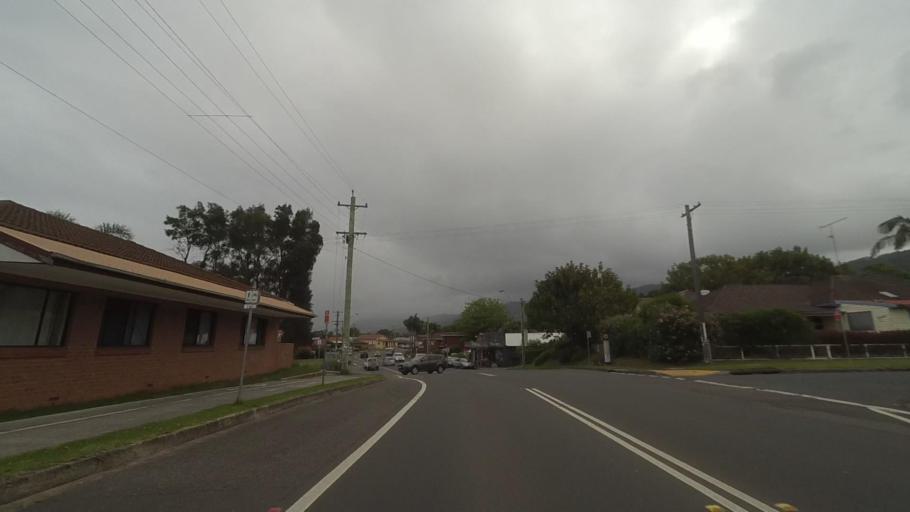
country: AU
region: New South Wales
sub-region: Wollongong
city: Bulli
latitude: -34.3134
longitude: 150.9272
